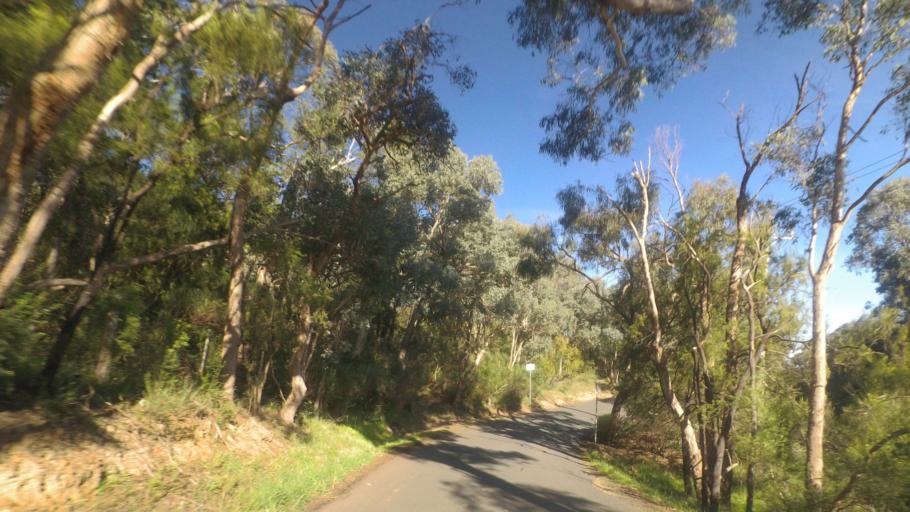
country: AU
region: Victoria
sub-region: Nillumbik
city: Research
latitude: -37.7023
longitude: 145.1949
